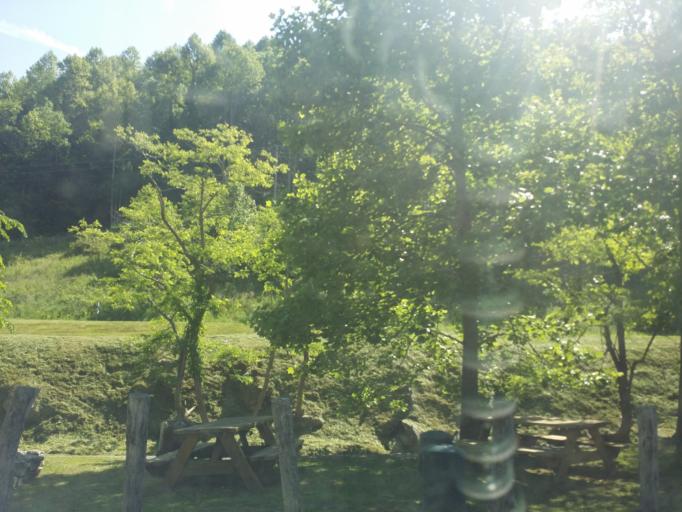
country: US
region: North Carolina
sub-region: Madison County
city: Marshall
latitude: 35.7520
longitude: -82.8696
